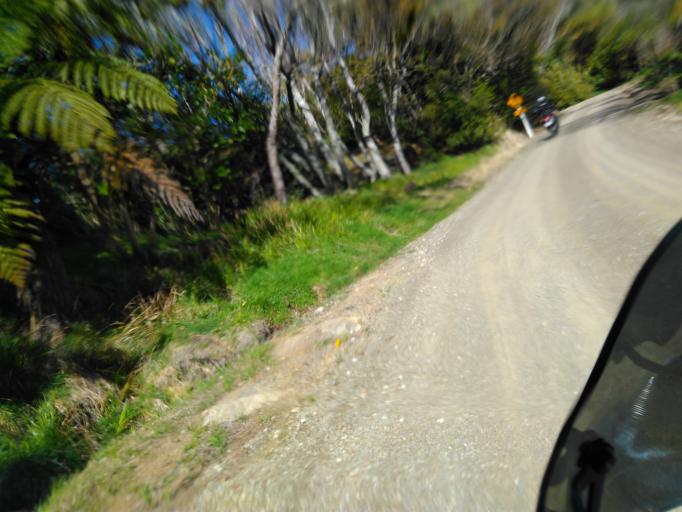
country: NZ
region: Bay of Plenty
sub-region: Opotiki District
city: Opotiki
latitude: -38.3710
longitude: 177.6015
